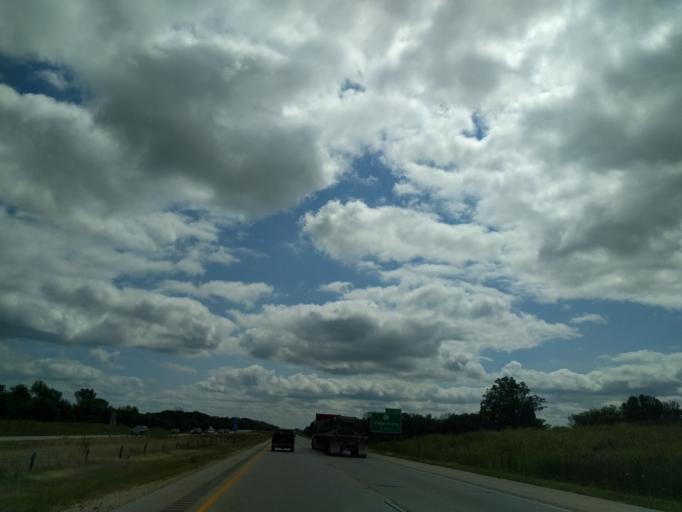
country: US
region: Wisconsin
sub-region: Ozaukee County
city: Grafton
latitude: 43.2996
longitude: -87.9207
